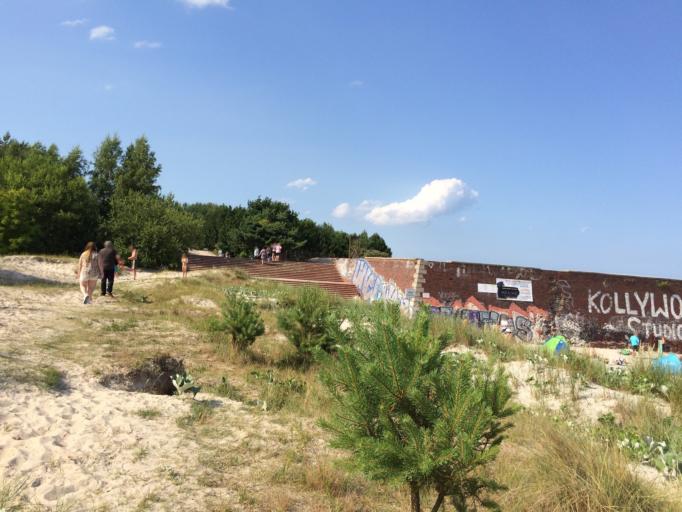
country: DE
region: Mecklenburg-Vorpommern
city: Ostseebad Binz
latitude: 54.4387
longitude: 13.5777
